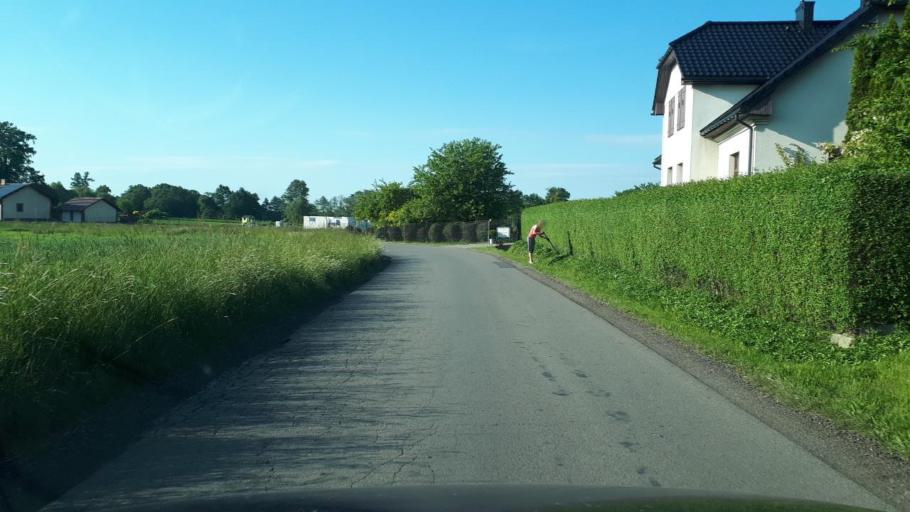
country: PL
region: Silesian Voivodeship
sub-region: Powiat bielski
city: Bronow
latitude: 49.8726
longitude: 18.9262
